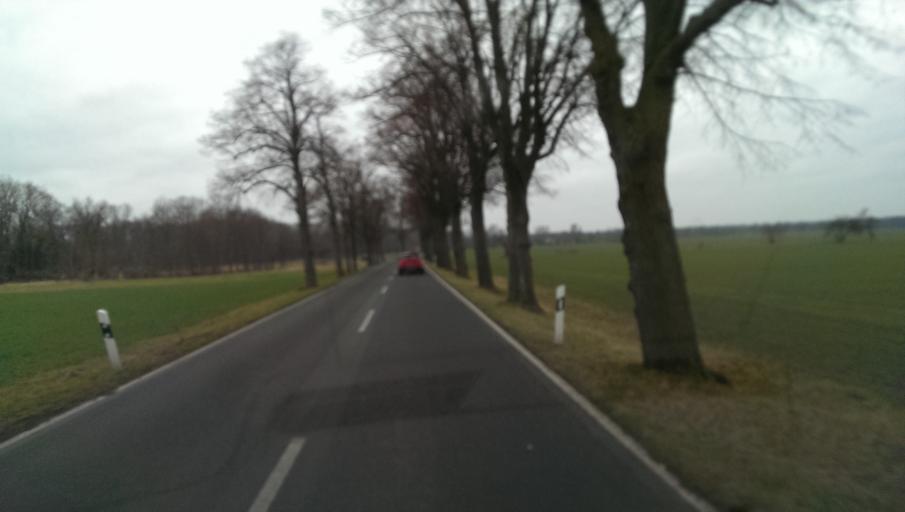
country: DE
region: Brandenburg
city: Ludwigsfelde
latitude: 52.2991
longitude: 13.3133
